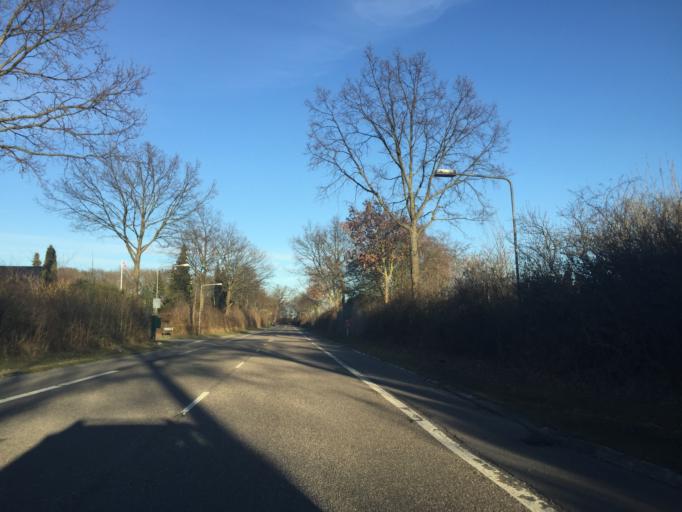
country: DK
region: Capital Region
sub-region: Dragor Kommune
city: Dragor
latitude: 55.5893
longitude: 12.6503
